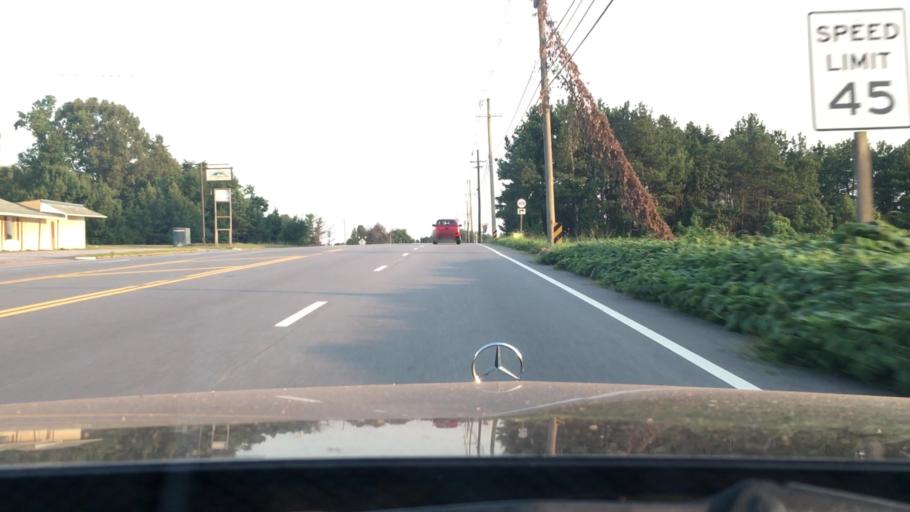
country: US
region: Virginia
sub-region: Pittsylvania County
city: Mount Hermon
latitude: 36.6698
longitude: -79.3744
